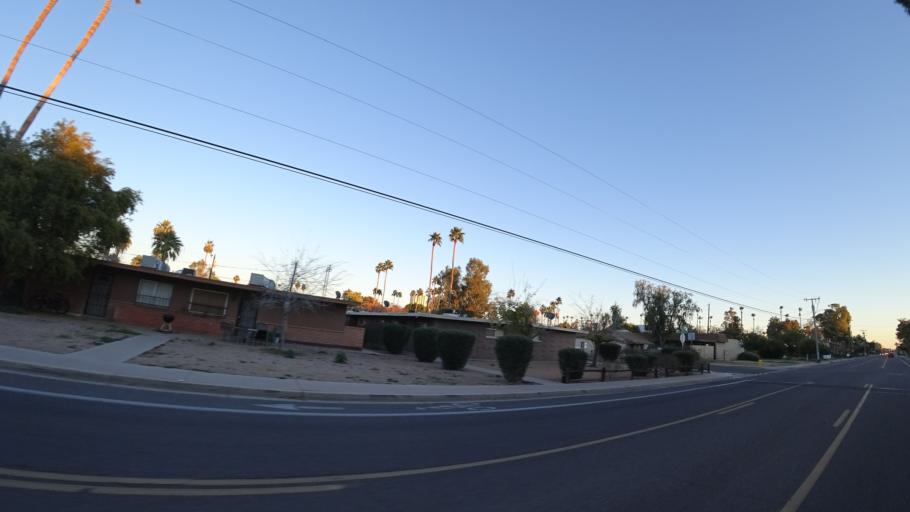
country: US
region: Arizona
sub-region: Maricopa County
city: Tempe Junction
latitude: 33.4281
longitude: -111.9524
